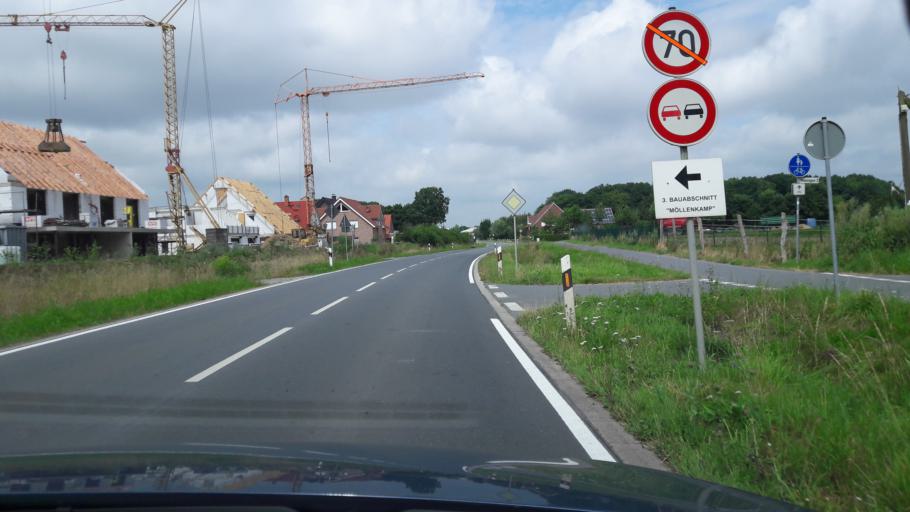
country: DE
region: North Rhine-Westphalia
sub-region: Regierungsbezirk Munster
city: Everswinkel
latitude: 51.9154
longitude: 7.8569
